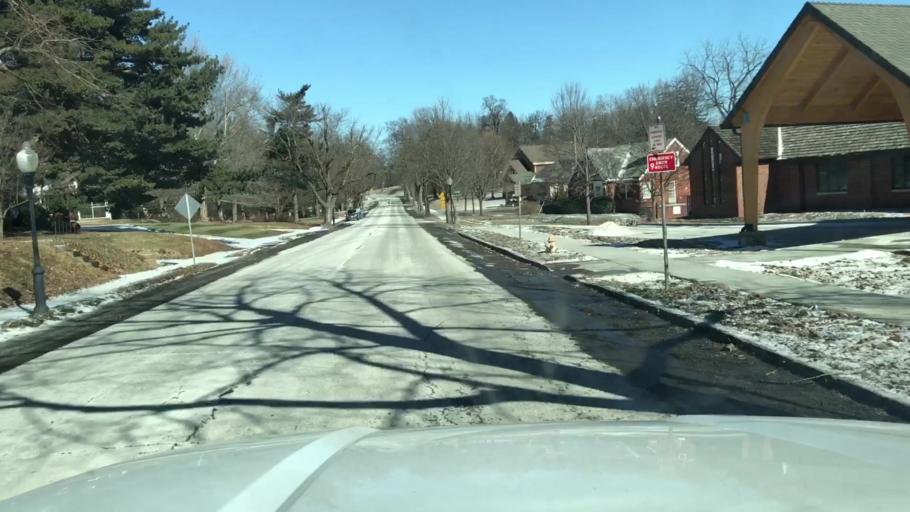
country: US
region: Missouri
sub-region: Buchanan County
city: Saint Joseph
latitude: 39.7925
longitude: -94.8208
